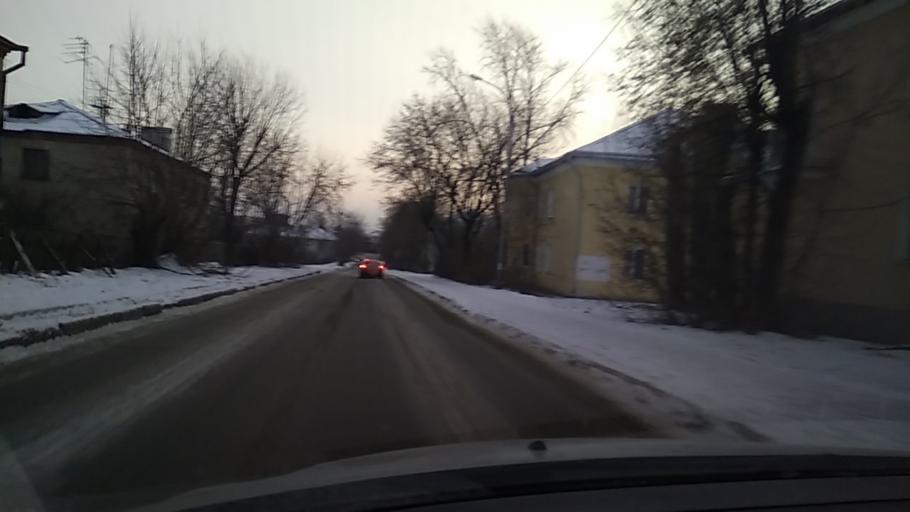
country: RU
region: Sverdlovsk
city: Istok
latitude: 56.7611
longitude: 60.7117
